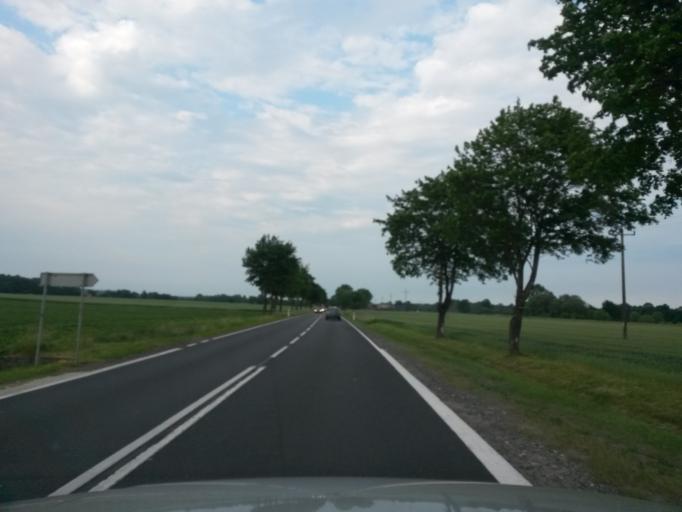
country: PL
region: Lower Silesian Voivodeship
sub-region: Powiat swidnicki
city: Strzegom
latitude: 50.9248
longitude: 16.2935
